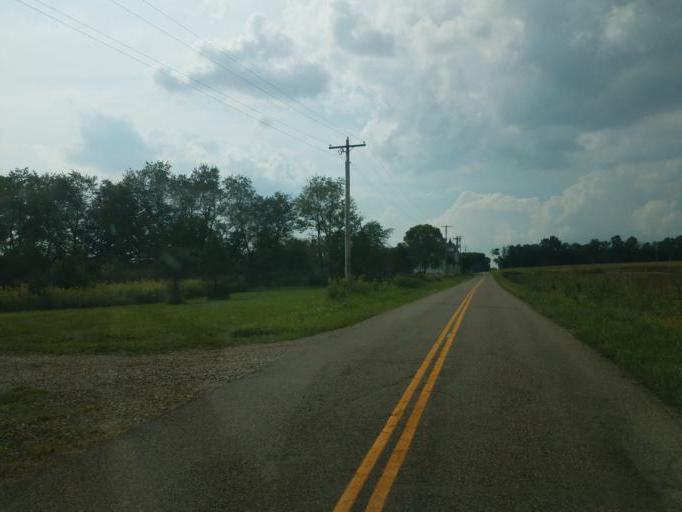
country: US
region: Ohio
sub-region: Knox County
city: Gambier
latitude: 40.3357
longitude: -82.3862
